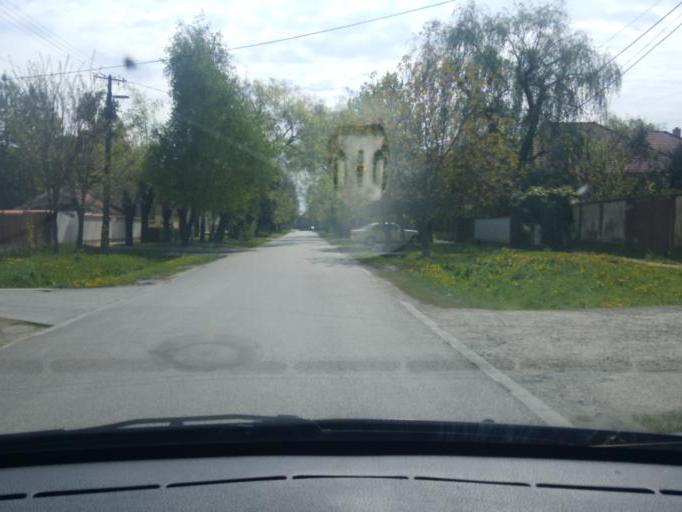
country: HU
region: Pest
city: Monor
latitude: 47.3472
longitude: 19.4446
